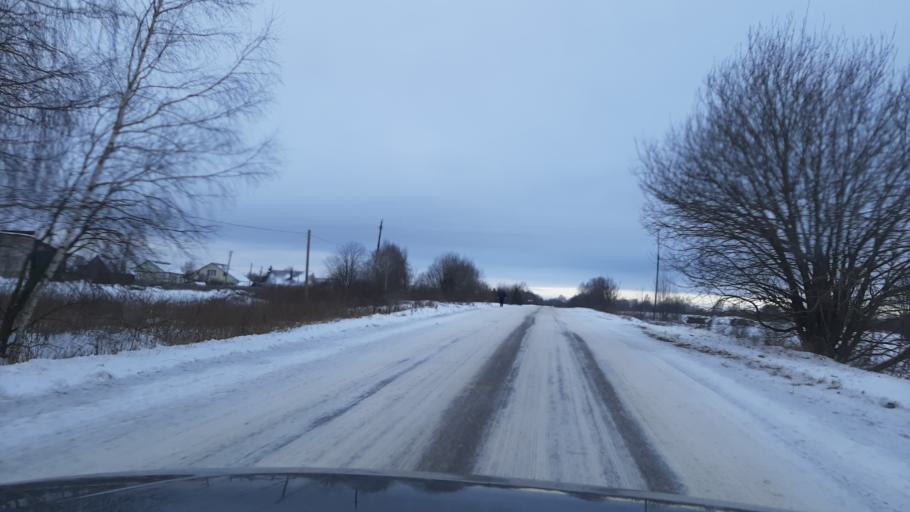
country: RU
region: Kostroma
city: Volgorechensk
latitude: 57.4352
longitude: 41.0634
